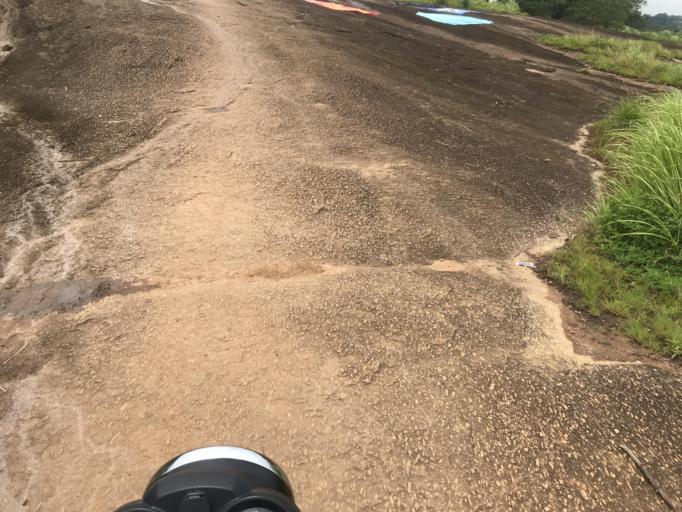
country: GN
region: Nzerekore
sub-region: Prefecture de Guekedou
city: Gueckedou
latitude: 8.4944
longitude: -10.3244
